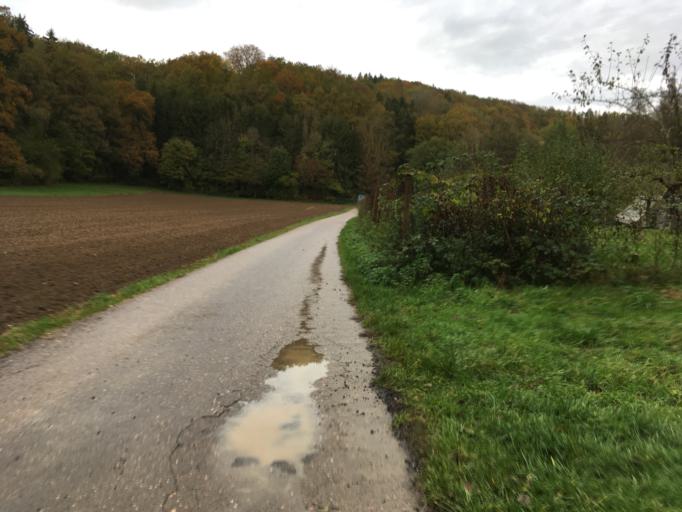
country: DE
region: Baden-Wuerttemberg
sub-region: Regierungsbezirk Stuttgart
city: Widdern
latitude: 49.3252
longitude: 9.4200
